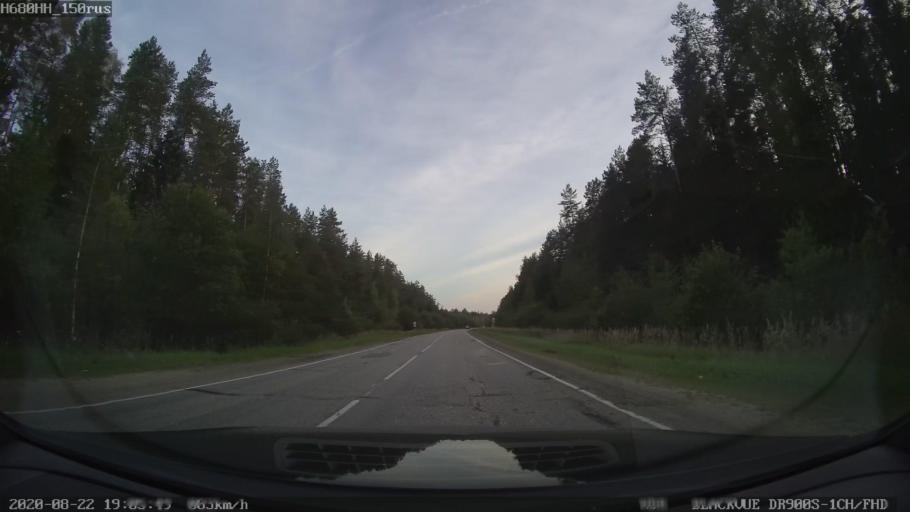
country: RU
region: Tverskaya
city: Sakharovo
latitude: 57.0715
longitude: 36.1102
